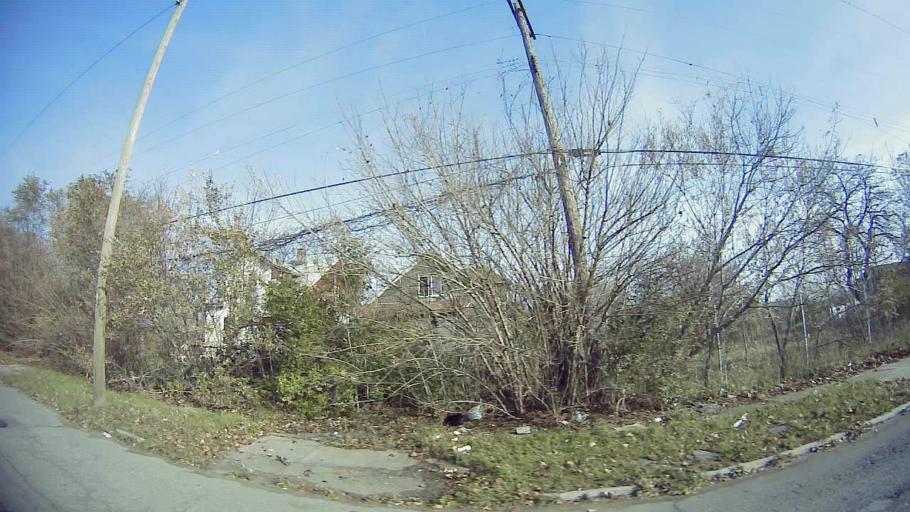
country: US
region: Michigan
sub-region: Oakland County
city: Hazel Park
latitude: 42.4407
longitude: -83.0944
